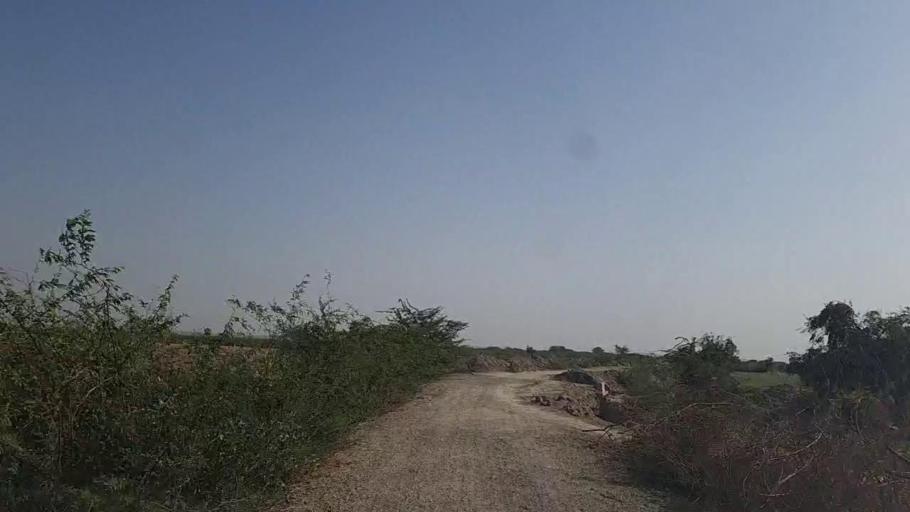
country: PK
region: Sindh
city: Kadhan
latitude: 24.5868
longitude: 69.2628
